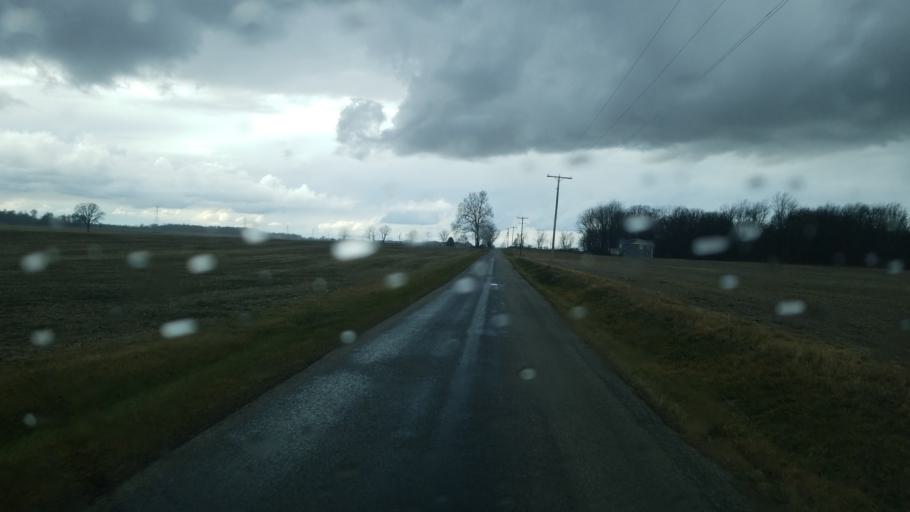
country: US
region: Ohio
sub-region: Crawford County
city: Crestline
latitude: 40.8577
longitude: -82.8405
